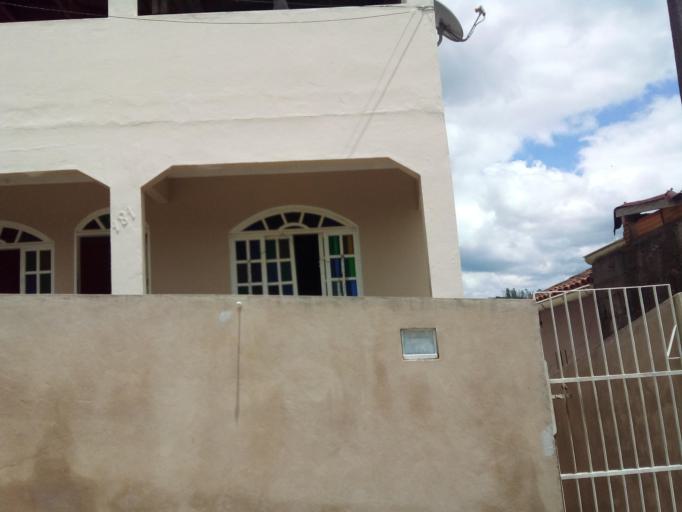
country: BR
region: Espirito Santo
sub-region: Fundao
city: Fundao
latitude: -19.9305
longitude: -40.4002
